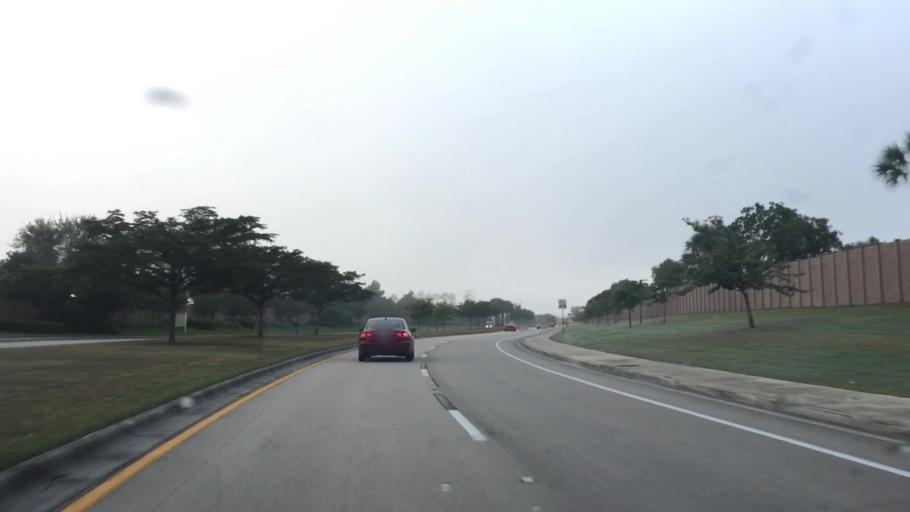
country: US
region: Florida
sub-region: Lee County
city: Gateway
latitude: 26.5925
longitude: -81.7839
